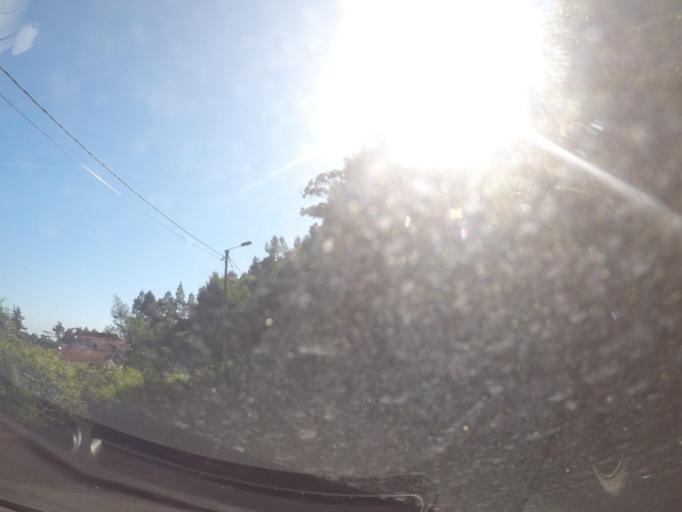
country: PT
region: Madeira
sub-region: Porto Moniz
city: Porto Moniz
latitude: 32.8514
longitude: -17.1690
